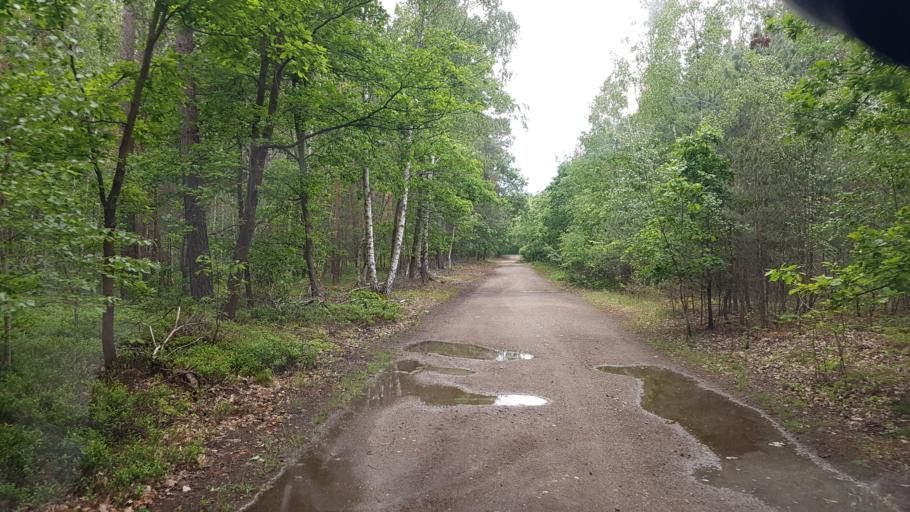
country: DE
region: Brandenburg
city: Hohenleipisch
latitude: 51.5283
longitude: 13.5411
